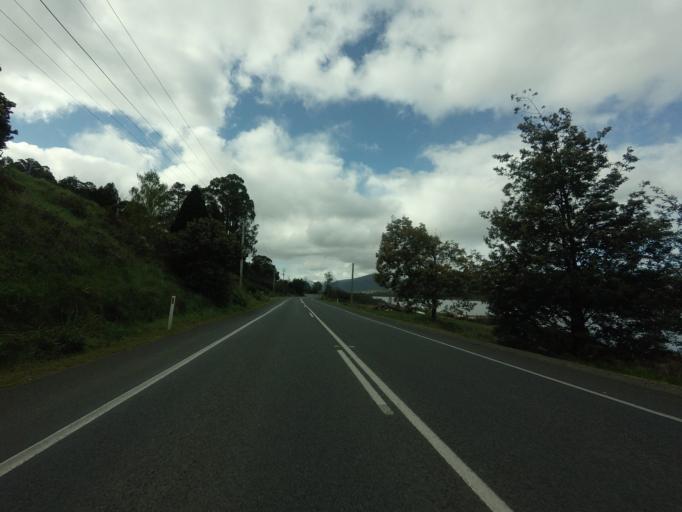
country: AU
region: Tasmania
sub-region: Huon Valley
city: Franklin
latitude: -43.1036
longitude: 147.0015
